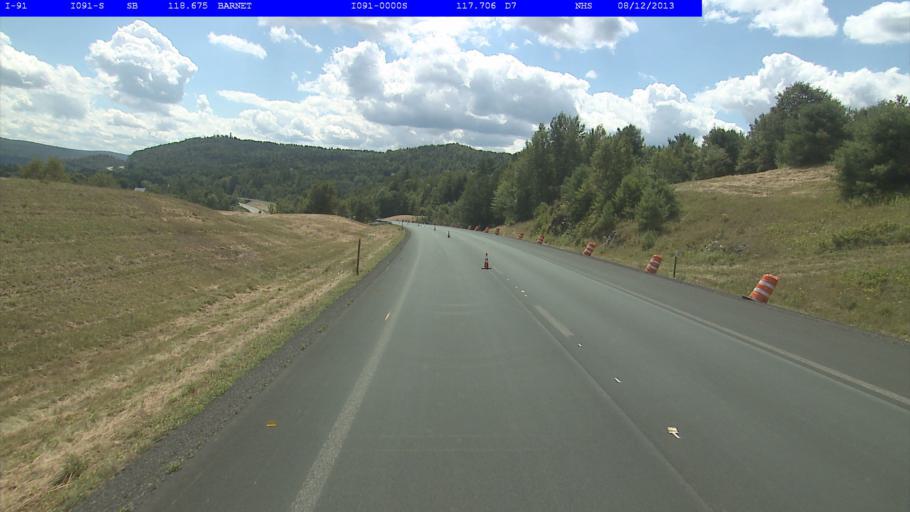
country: US
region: New Hampshire
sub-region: Grafton County
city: Woodsville
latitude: 44.2754
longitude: -72.0725
